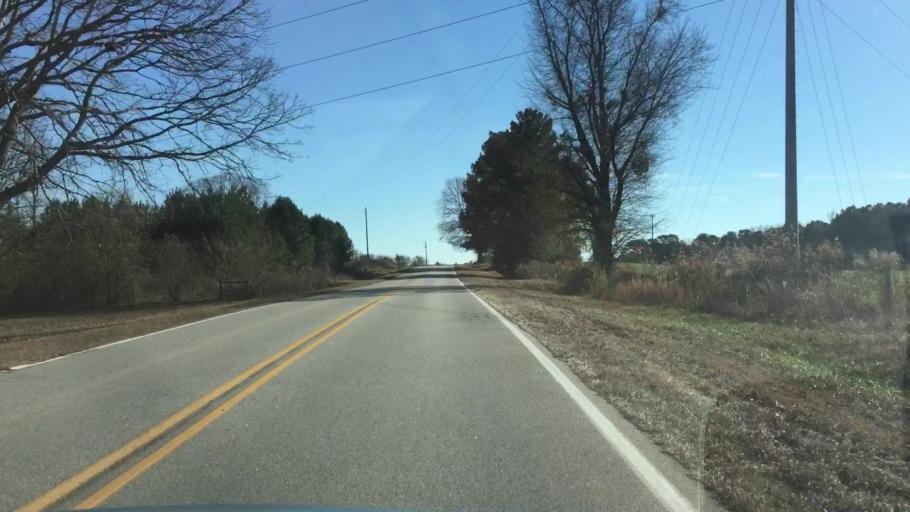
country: US
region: Georgia
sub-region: Newton County
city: Oakwood
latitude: 33.4970
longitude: -84.0479
